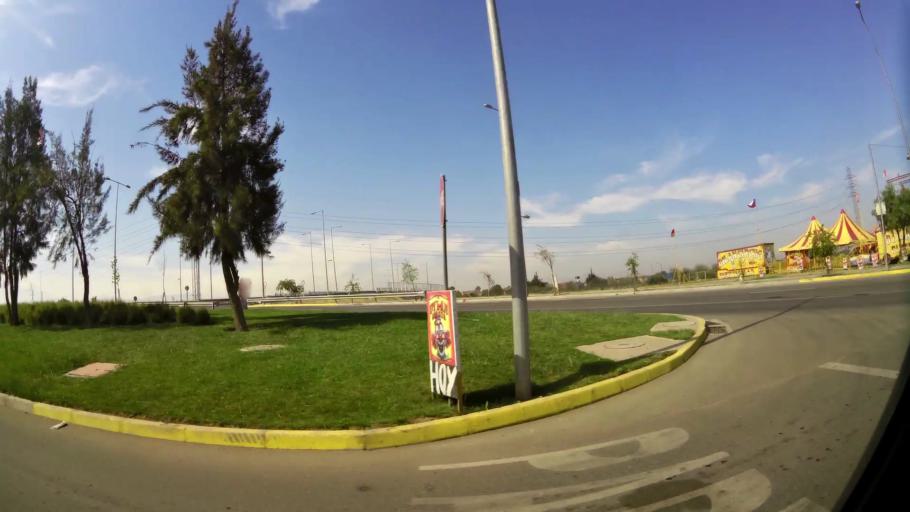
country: CL
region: Santiago Metropolitan
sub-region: Provincia de Santiago
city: Lo Prado
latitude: -33.4838
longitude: -70.7431
